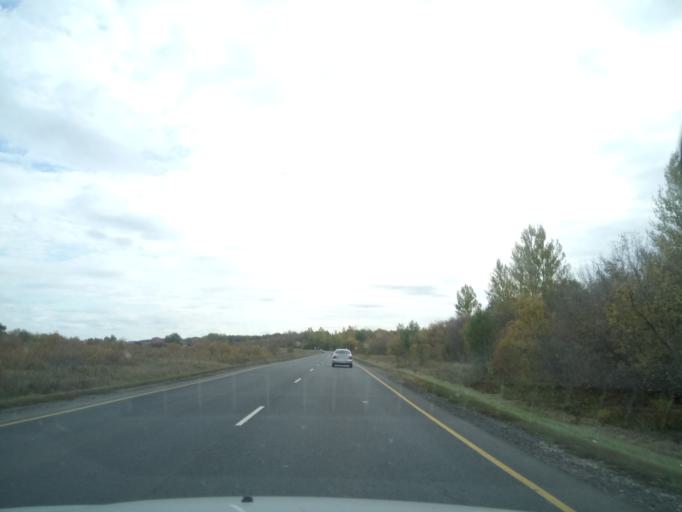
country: RU
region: Nizjnij Novgorod
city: Lukoyanov
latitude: 55.0529
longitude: 44.3731
